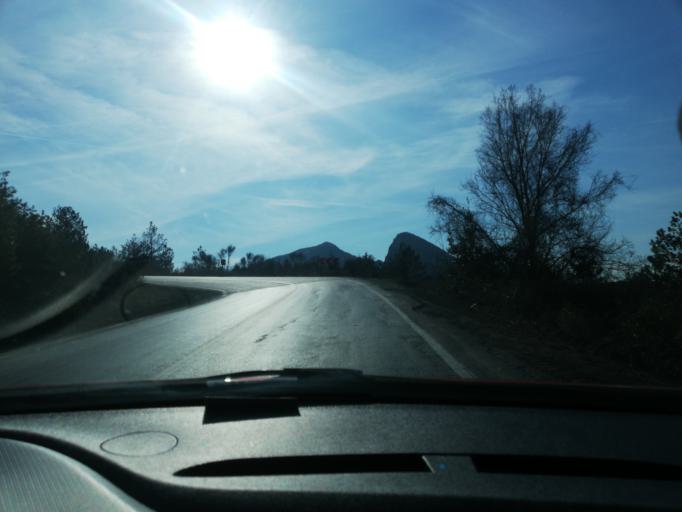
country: TR
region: Bartin
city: Kurucasile
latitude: 41.8451
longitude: 32.7622
